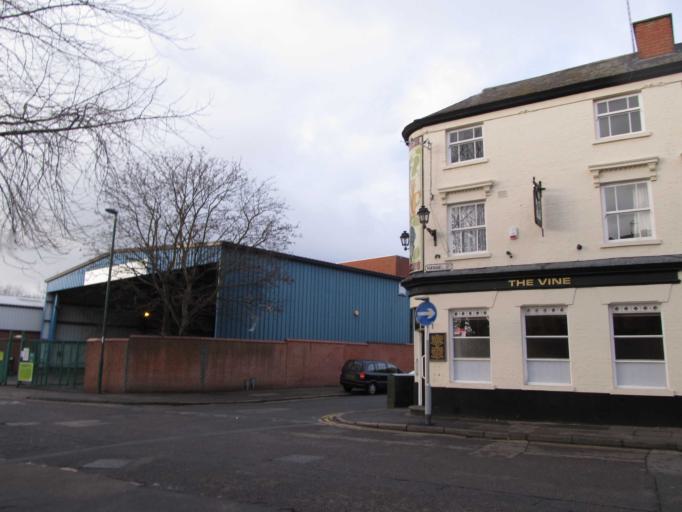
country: GB
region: England
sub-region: Nottingham
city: Nottingham
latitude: 52.9552
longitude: -1.1362
